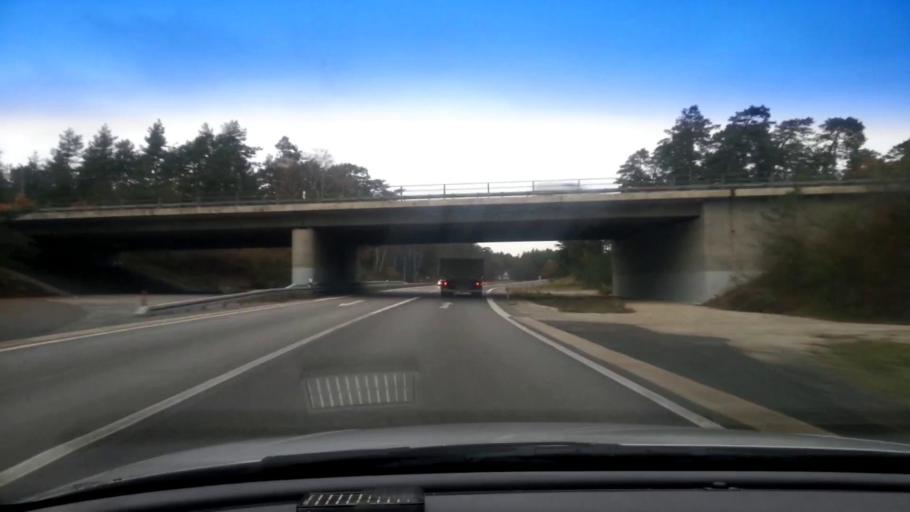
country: DE
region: Bavaria
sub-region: Upper Franconia
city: Strullendorf
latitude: 49.8704
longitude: 10.9459
